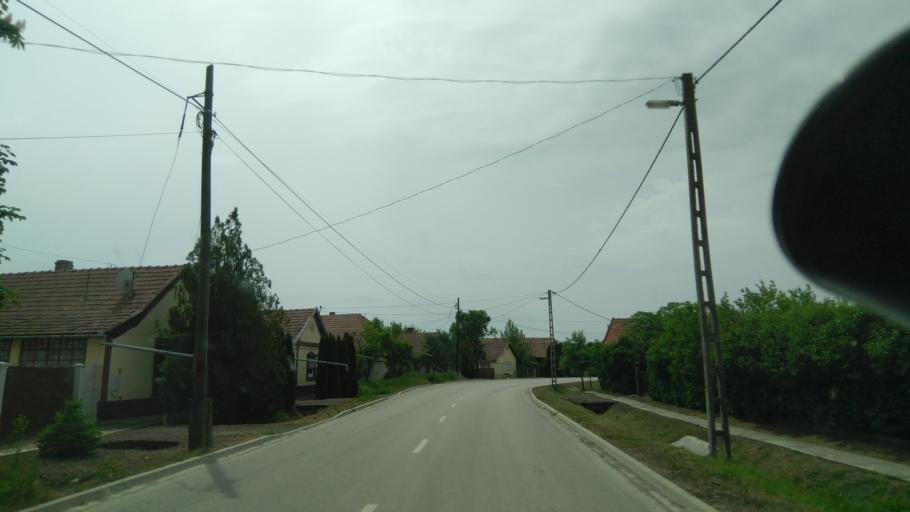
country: HU
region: Bekes
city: Mehkerek
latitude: 46.8665
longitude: 21.5181
